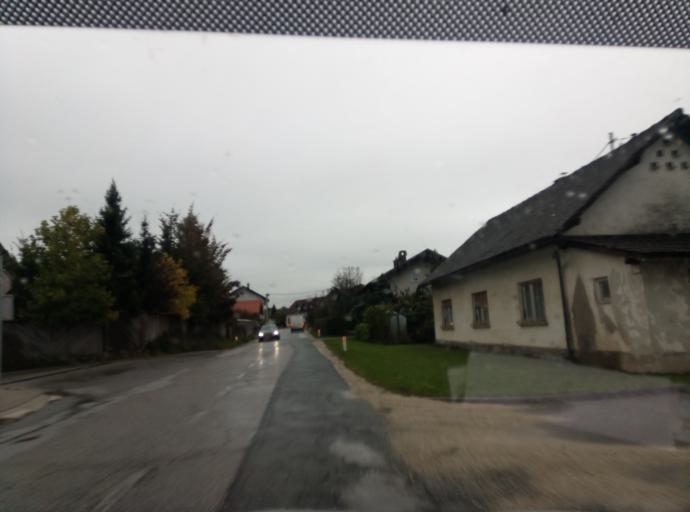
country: SI
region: Medvode
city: Zgornje Pirnice
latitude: 46.1281
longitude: 14.4766
